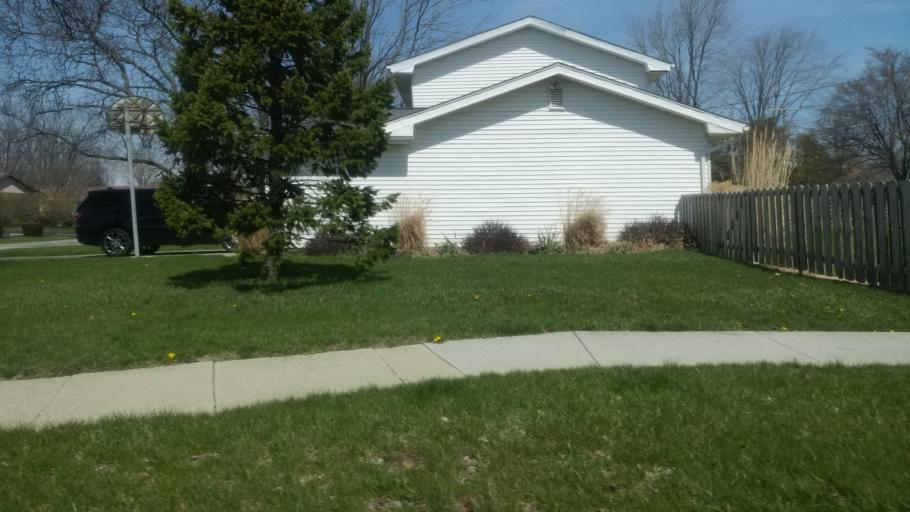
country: US
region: Ohio
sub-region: Wood County
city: Bowling Green
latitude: 41.3862
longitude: -83.6628
